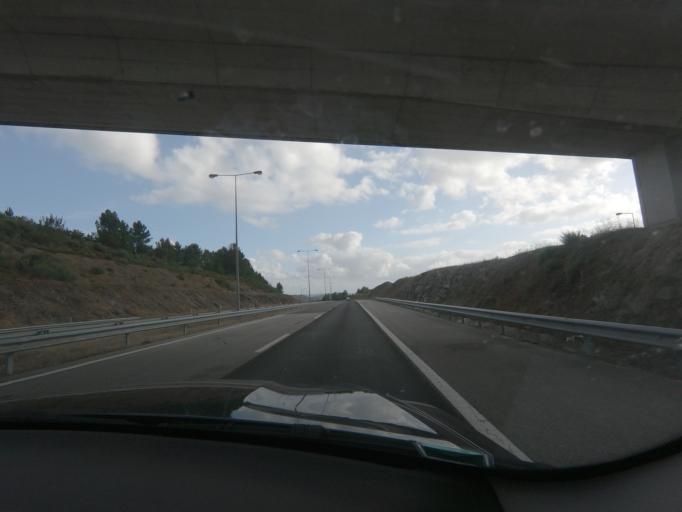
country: PT
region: Viseu
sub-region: Castro Daire
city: Castro Daire
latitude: 40.8614
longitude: -7.9281
